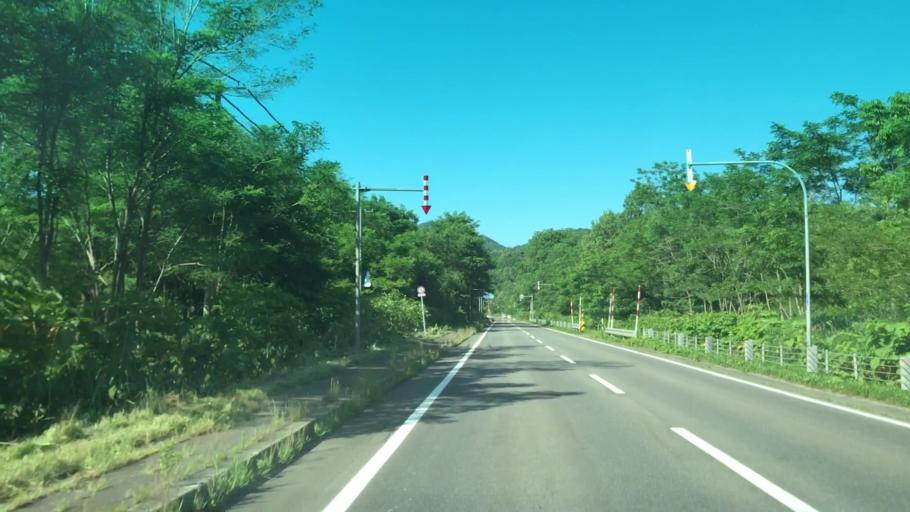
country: JP
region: Hokkaido
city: Iwanai
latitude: 42.9922
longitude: 140.6635
